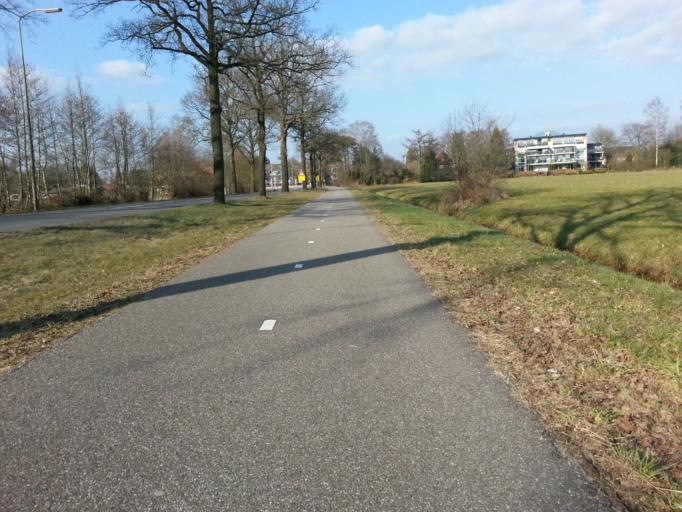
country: NL
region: Utrecht
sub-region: Gemeente Amersfoort
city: Randenbroek
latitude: 52.1192
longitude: 5.4024
